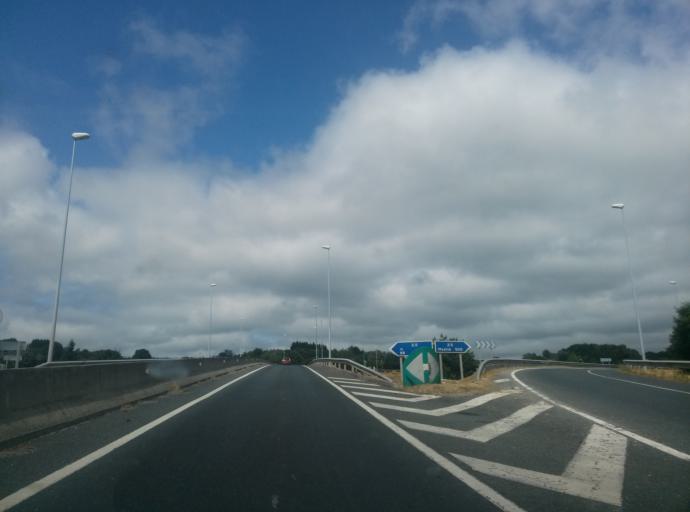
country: ES
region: Galicia
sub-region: Provincia de Lugo
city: Lugo
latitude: 43.0567
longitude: -7.5614
